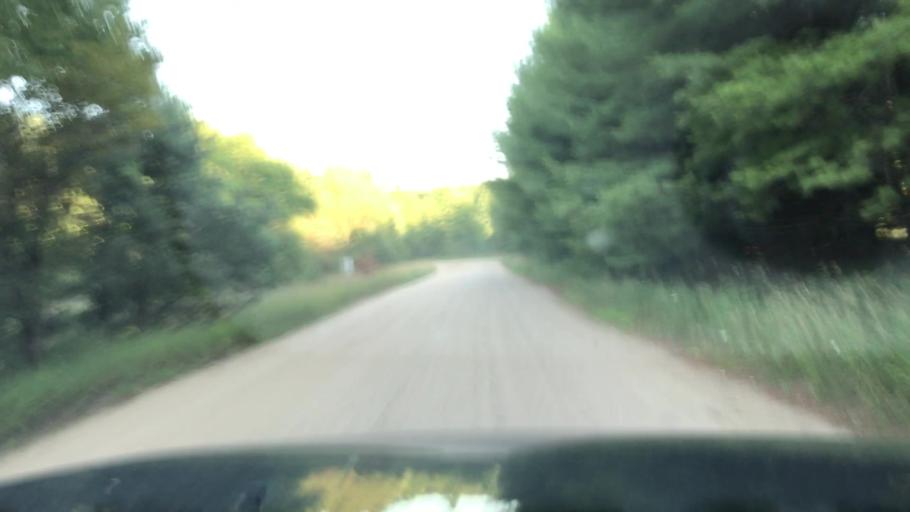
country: US
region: Michigan
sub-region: Osceola County
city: Evart
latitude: 43.8659
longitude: -85.3620
